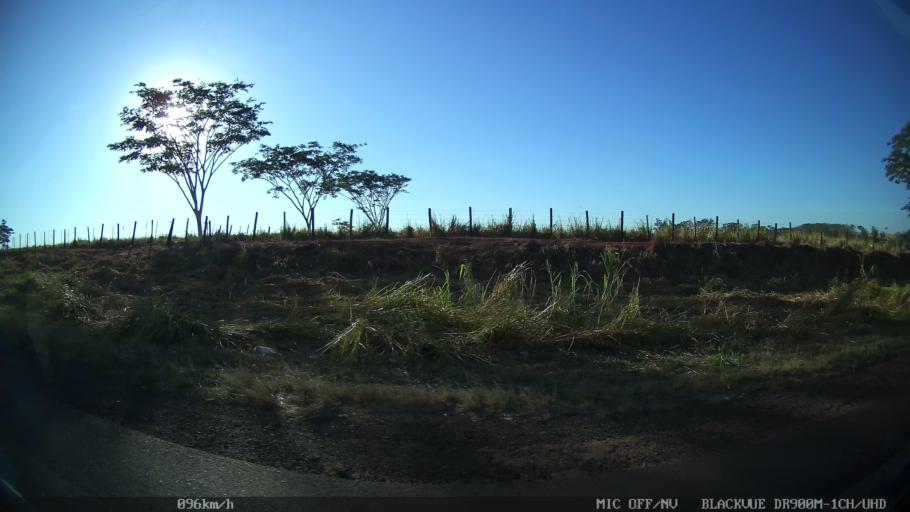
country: BR
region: Sao Paulo
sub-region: Guapiacu
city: Guapiacu
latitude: -20.7673
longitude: -49.2027
